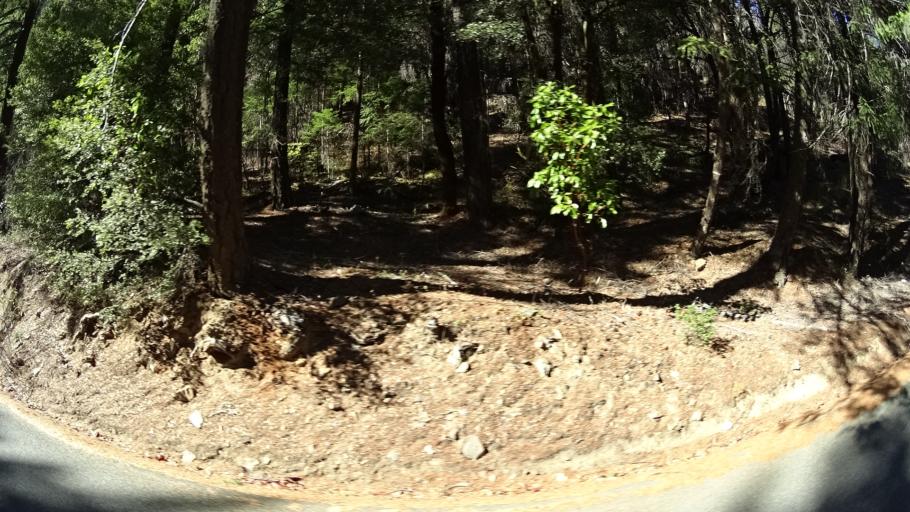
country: US
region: California
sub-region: Siskiyou County
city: Happy Camp
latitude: 41.3383
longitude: -123.0468
